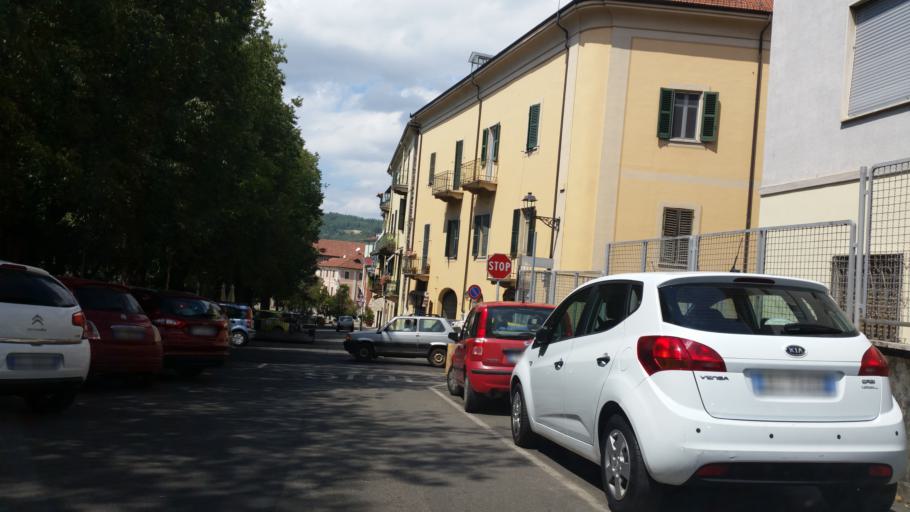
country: IT
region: Piedmont
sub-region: Provincia di Alessandria
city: Acqui Terme
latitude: 44.6757
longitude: 8.4728
